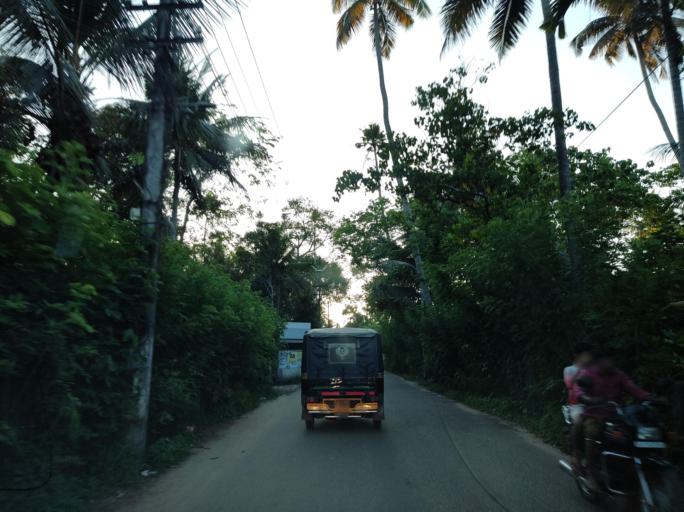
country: IN
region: Kerala
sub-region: Alappuzha
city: Vayalar
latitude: 9.7054
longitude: 76.3021
